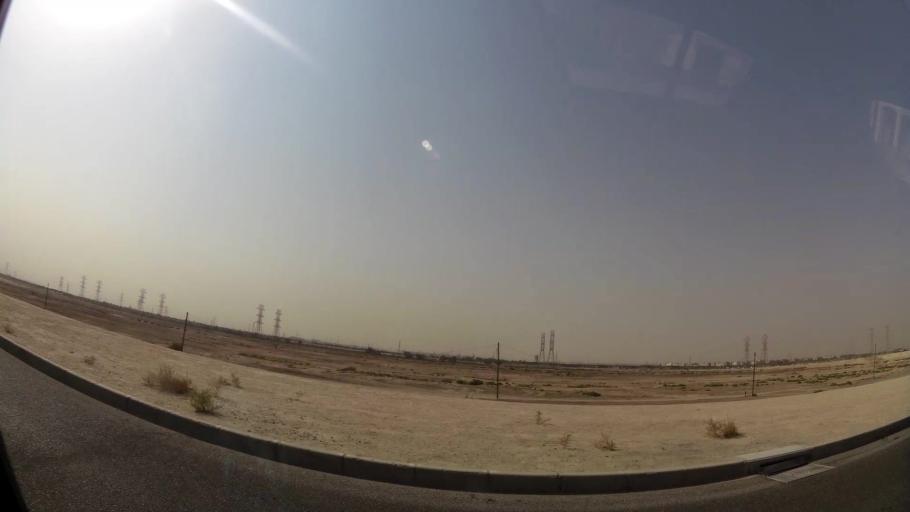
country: KW
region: Muhafazat al Jahra'
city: Al Jahra'
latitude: 29.3316
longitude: 47.7607
